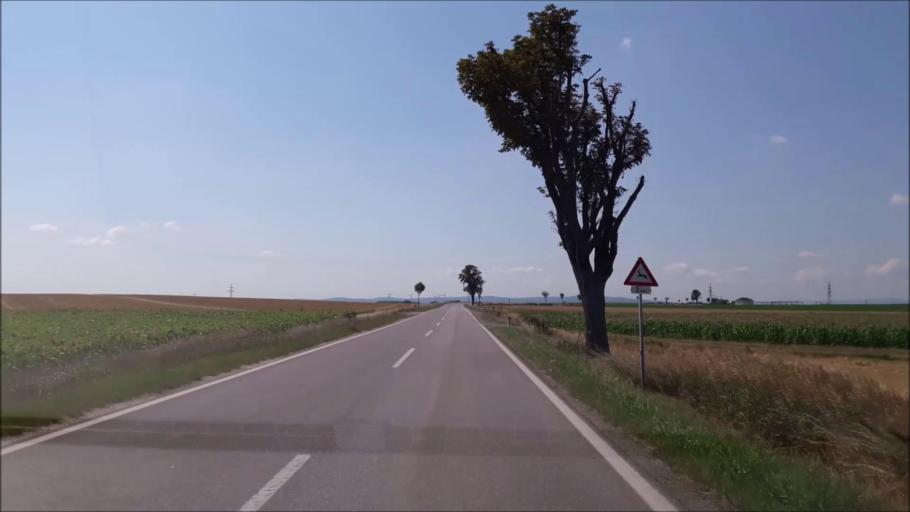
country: AT
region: Lower Austria
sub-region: Politischer Bezirk Wien-Umgebung
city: Moosbrunn
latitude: 48.0374
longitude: 16.4655
